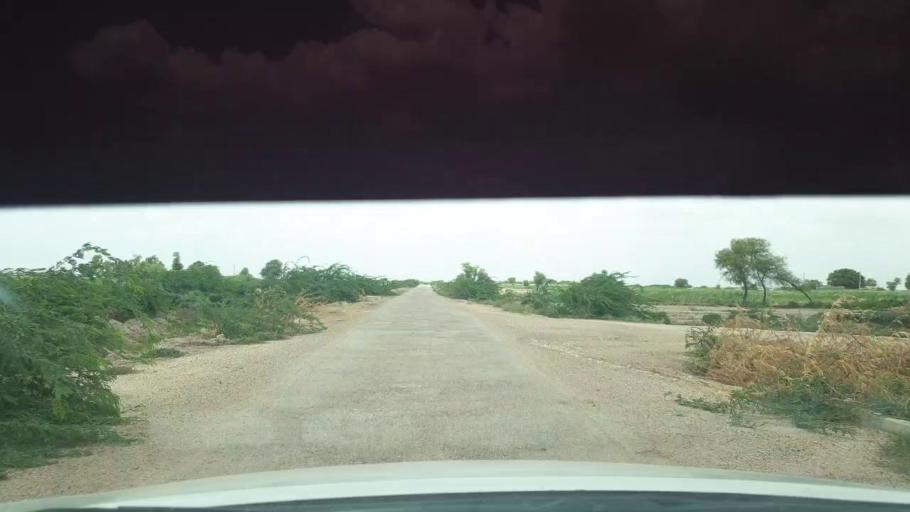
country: PK
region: Sindh
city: Kadhan
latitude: 24.5378
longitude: 69.1247
